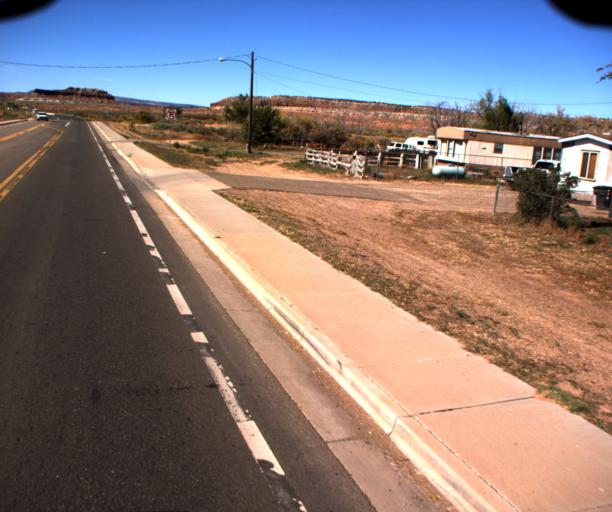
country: US
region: Arizona
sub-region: Coconino County
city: Fredonia
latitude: 36.9457
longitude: -112.5318
